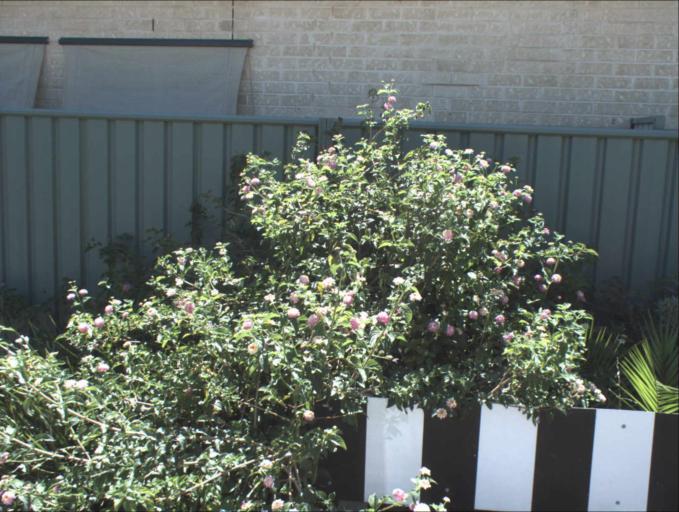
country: AU
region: South Australia
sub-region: Port Adelaide Enfield
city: Klemzig
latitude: -34.8833
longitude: 138.6443
